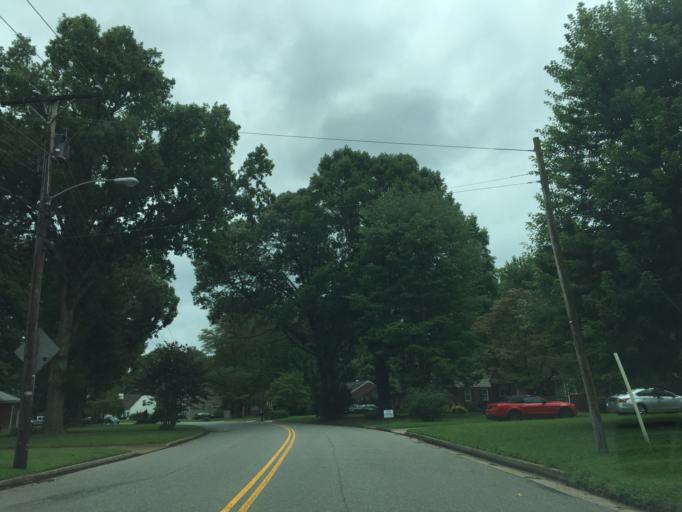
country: US
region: Virginia
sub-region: City of Newport News
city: Newport News
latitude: 37.0663
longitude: -76.5037
